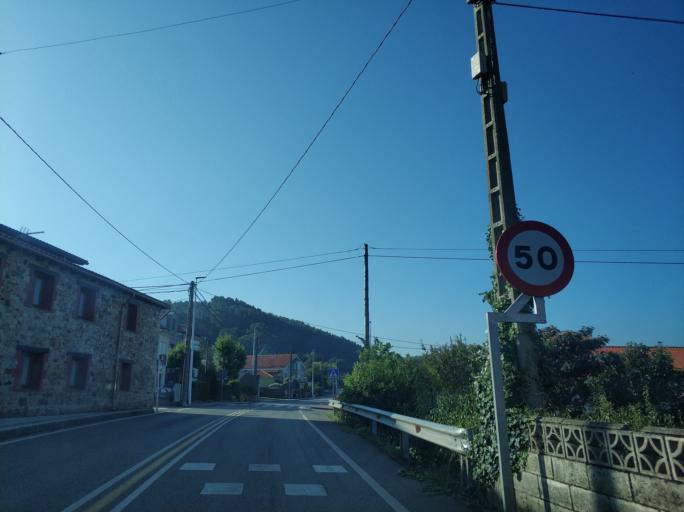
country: ES
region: Cantabria
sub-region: Provincia de Cantabria
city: Polanco
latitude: 43.3700
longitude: -3.9598
